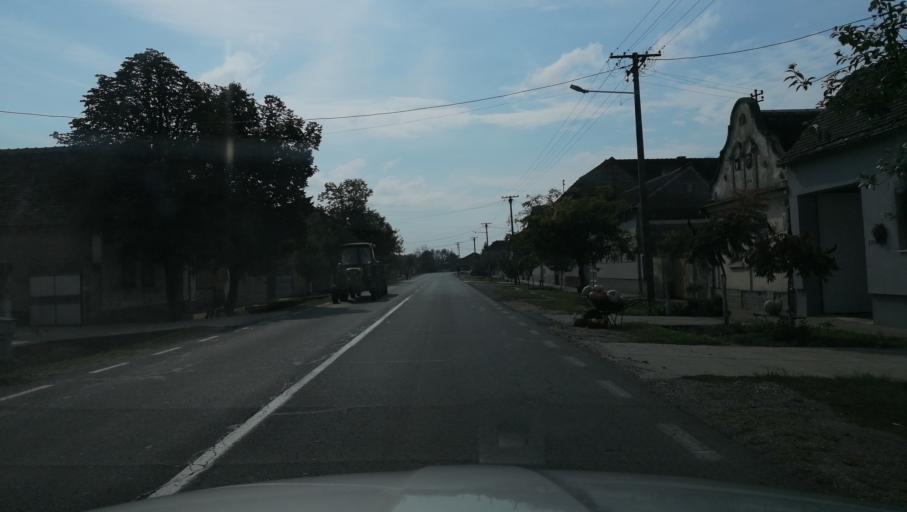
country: RS
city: Ravnje
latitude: 45.0170
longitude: 19.4000
